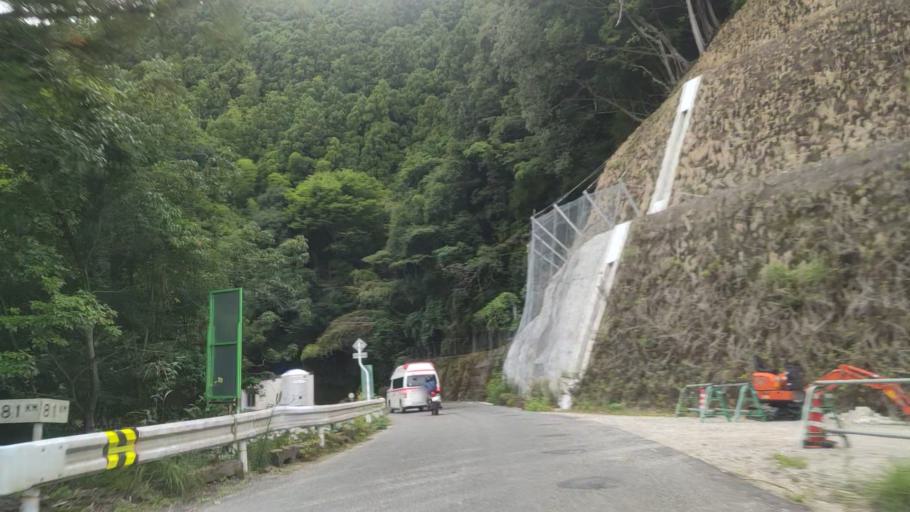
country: JP
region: Wakayama
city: Koya
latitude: 34.2239
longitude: 135.5389
